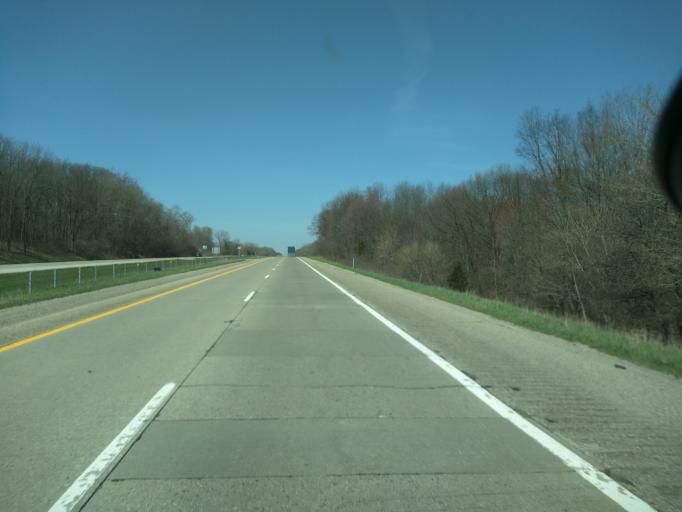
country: US
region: Michigan
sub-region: Kent County
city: Lowell
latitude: 42.8788
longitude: -85.3827
